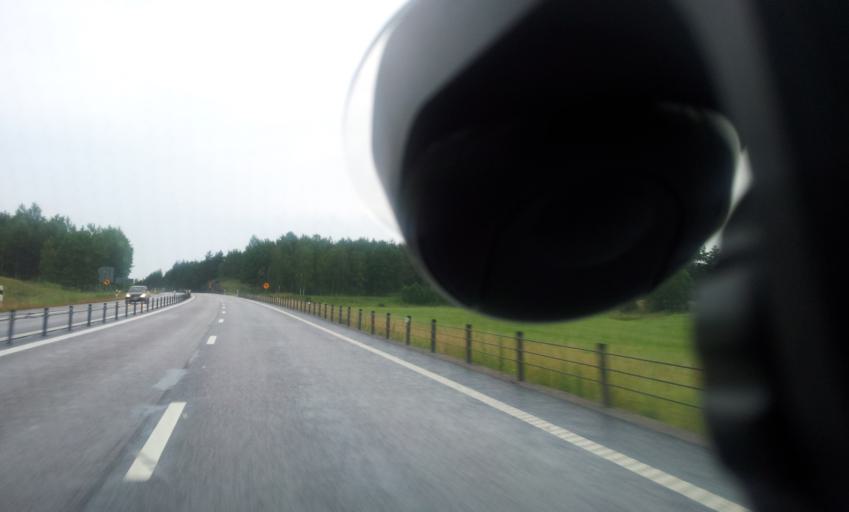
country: SE
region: OEstergoetland
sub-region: Valdemarsviks Kommun
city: Valdemarsvik
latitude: 58.2290
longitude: 16.5525
